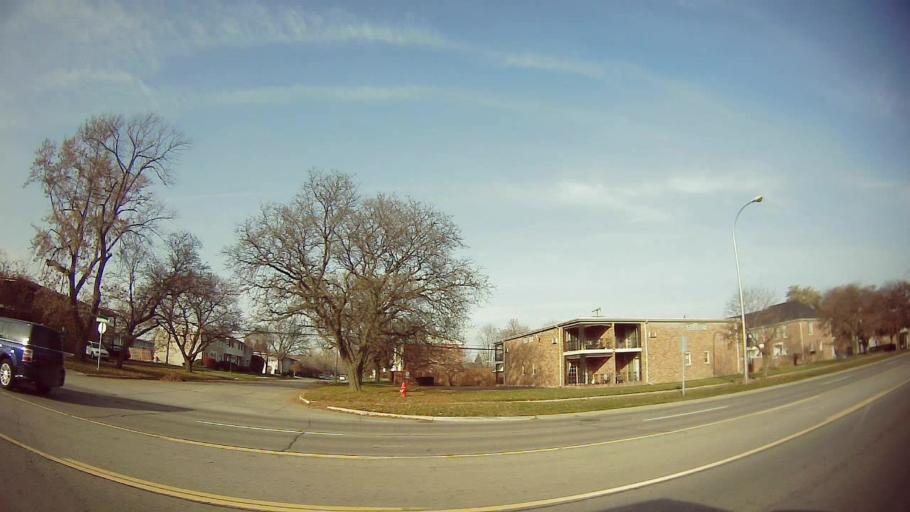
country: US
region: Michigan
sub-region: Oakland County
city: Clawson
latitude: 42.5328
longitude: -83.1727
